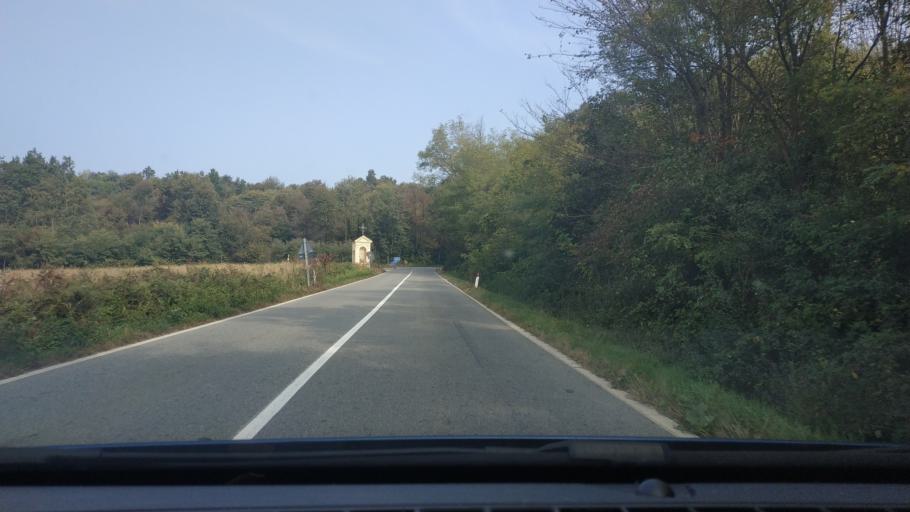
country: IT
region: Piedmont
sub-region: Provincia di Torino
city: Montalenghe
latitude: 45.3467
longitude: 7.8383
